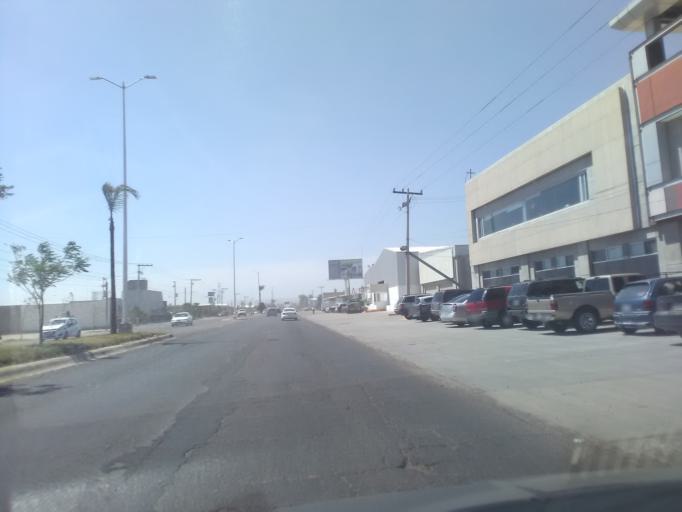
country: MX
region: Durango
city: Victoria de Durango
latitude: 24.0296
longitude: -104.6052
